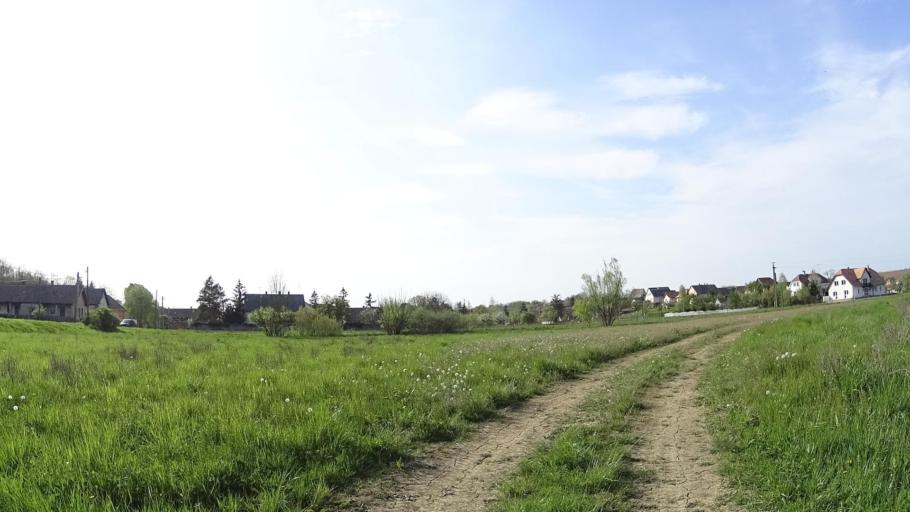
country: HU
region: Nograd
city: Romhany
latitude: 47.8856
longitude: 19.1997
